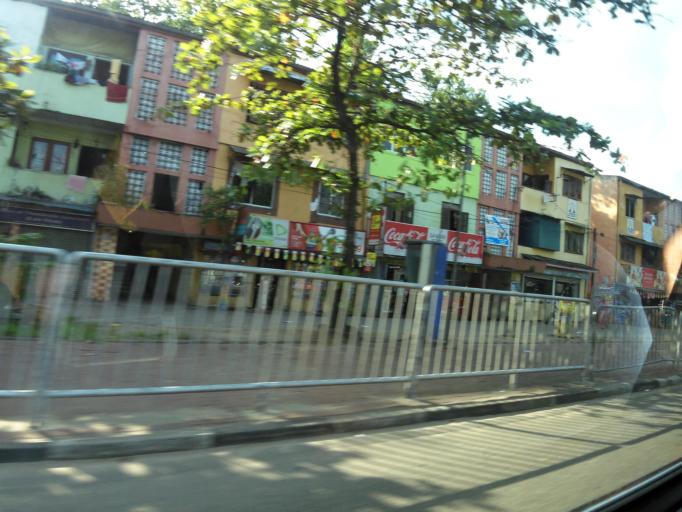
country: LK
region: Western
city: Kolonnawa
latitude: 6.9439
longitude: 79.8782
